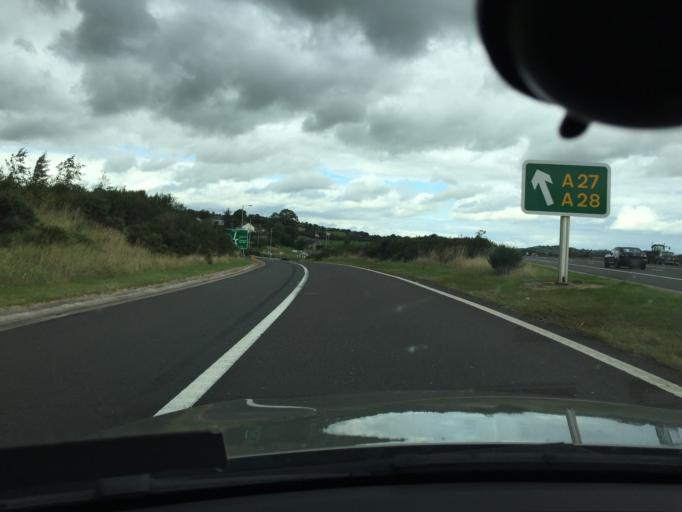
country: GB
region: Northern Ireland
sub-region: Newry and Mourne District
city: Newry
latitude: 54.1980
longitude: -6.3613
